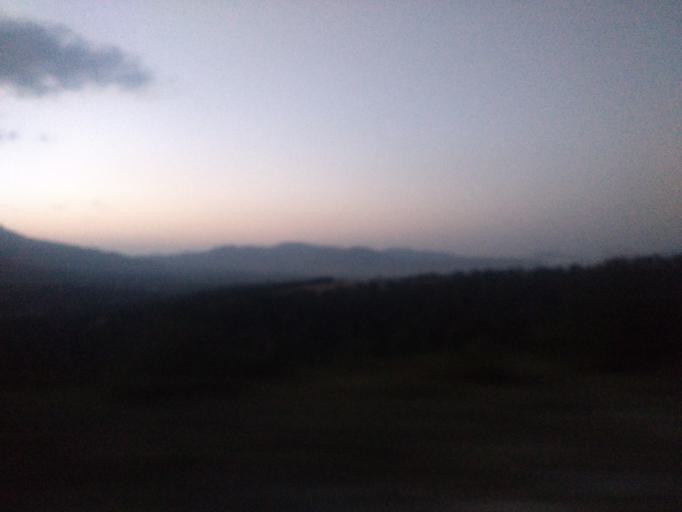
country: MX
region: Puebla
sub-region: Oriental
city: San Antonio Virreyes
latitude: 19.3953
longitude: -97.6837
